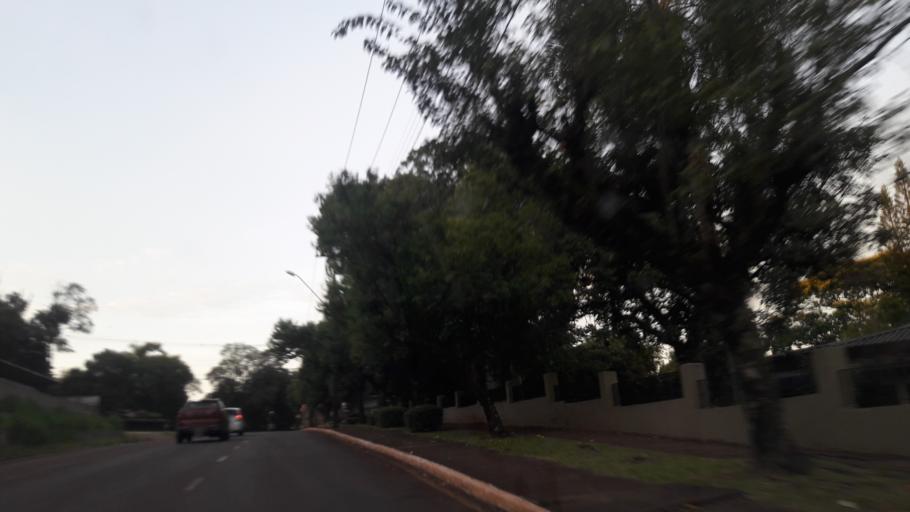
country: BR
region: Parana
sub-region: Cascavel
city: Cascavel
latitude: -24.9580
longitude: -53.4498
